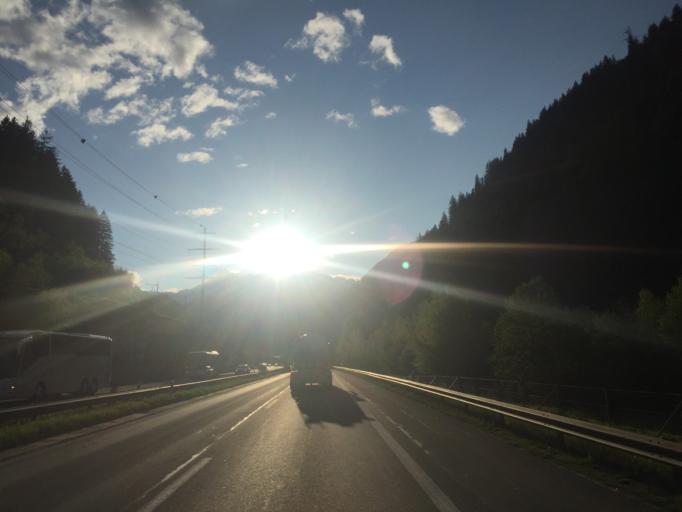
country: CH
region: Ticino
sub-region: Leventina District
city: Airolo
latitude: 46.5172
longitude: 8.6572
